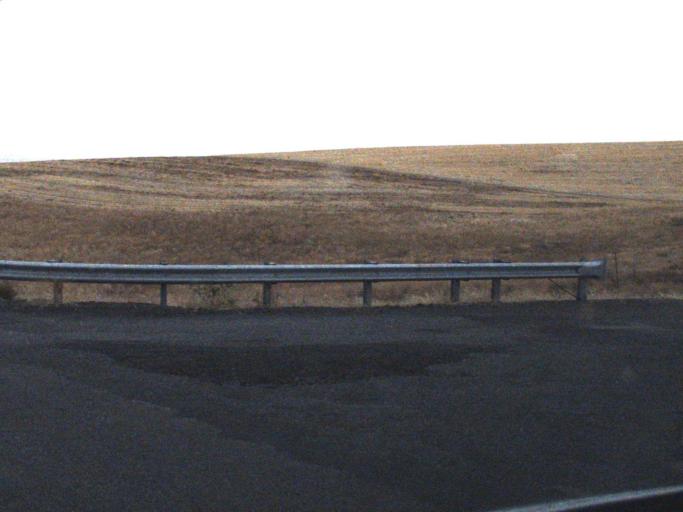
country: US
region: Washington
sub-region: Adams County
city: Ritzville
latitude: 46.7667
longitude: -118.3420
